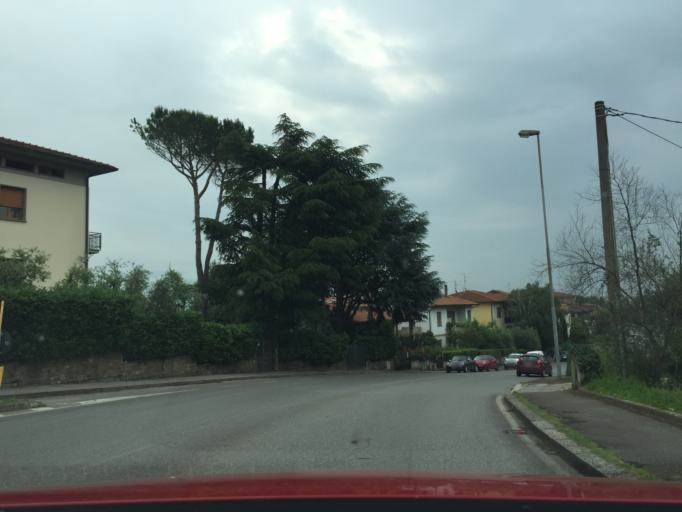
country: IT
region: Tuscany
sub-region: Provincia di Pistoia
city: Pistoia
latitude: 43.9454
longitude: 10.9080
